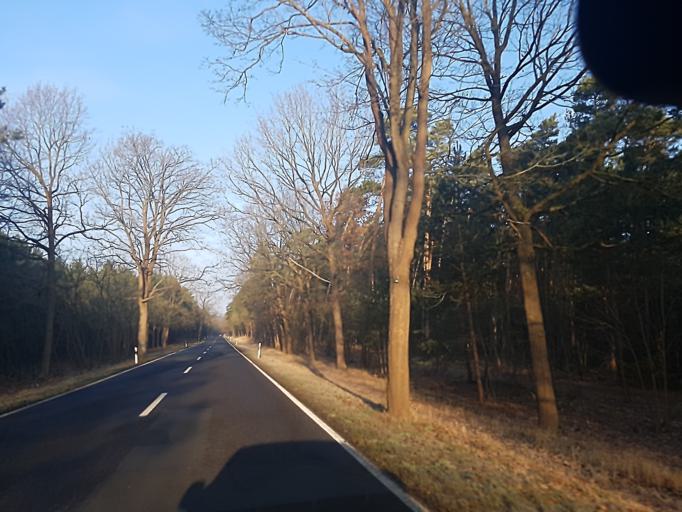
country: DE
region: Brandenburg
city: Bruck
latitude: 52.2196
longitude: 12.7344
